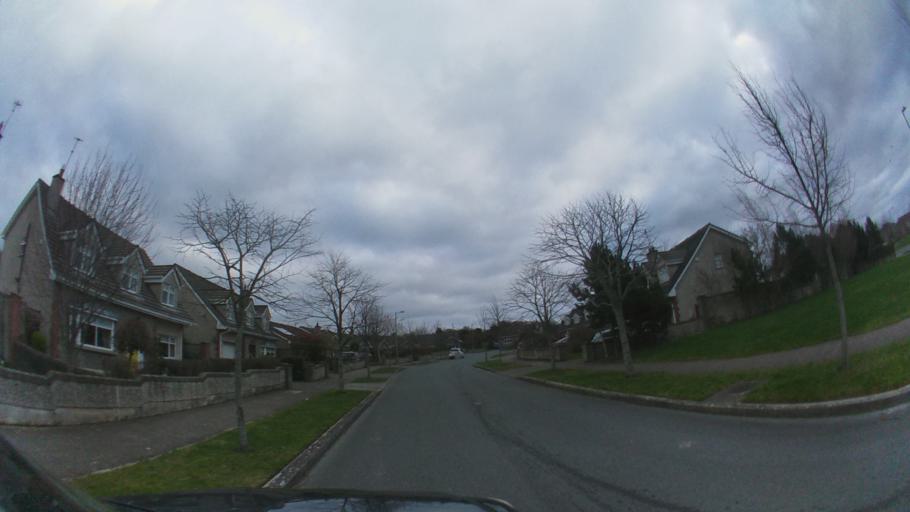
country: IE
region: Leinster
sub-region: An Mhi
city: Duleek
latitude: 53.6931
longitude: -6.4137
